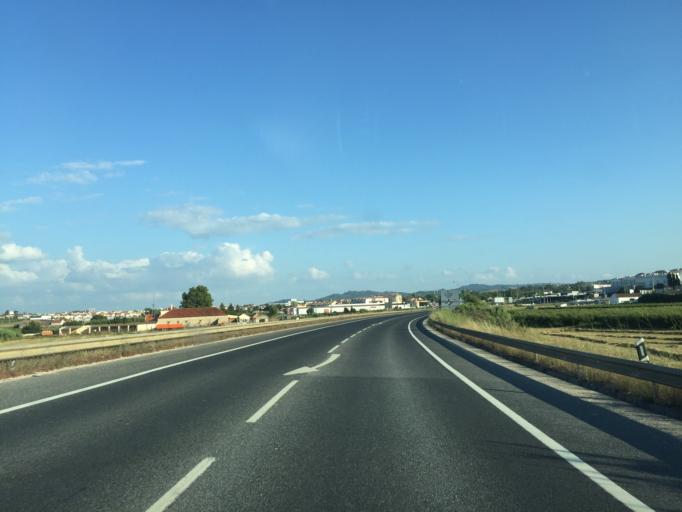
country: PT
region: Lisbon
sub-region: Alenquer
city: Alenquer
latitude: 39.0538
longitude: -8.9946
